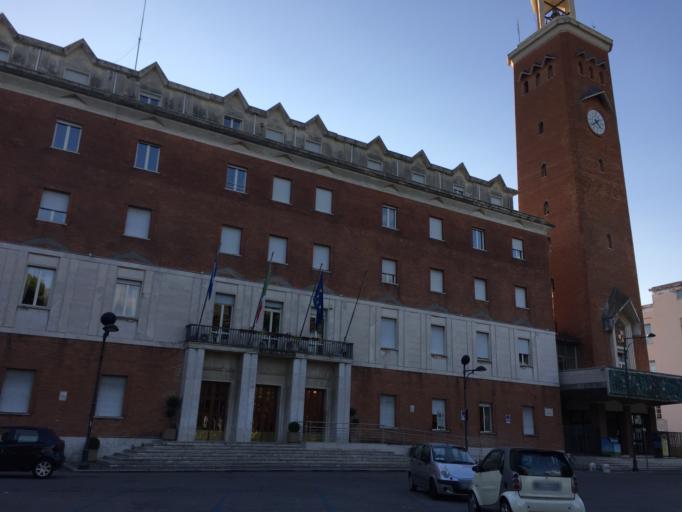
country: IT
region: Latium
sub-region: Provincia di Latina
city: Gaeta
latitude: 41.2136
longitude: 13.5721
